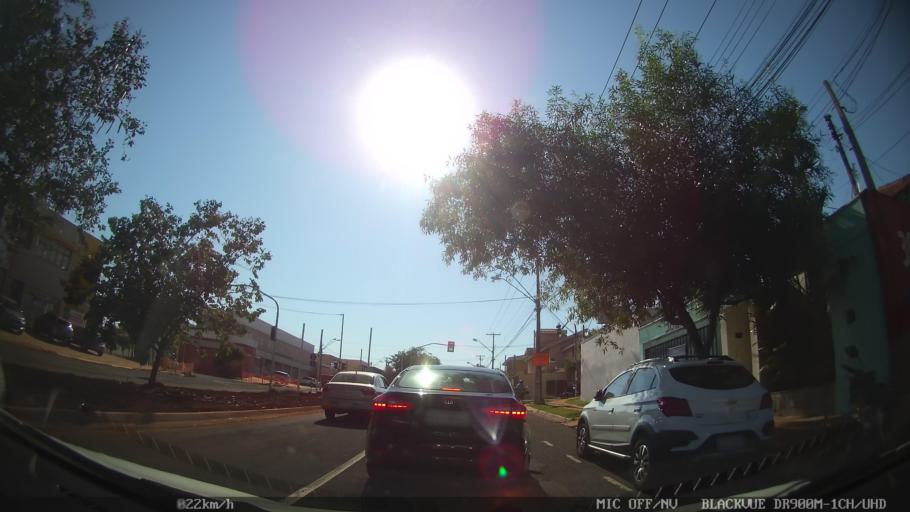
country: BR
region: Sao Paulo
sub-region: Ribeirao Preto
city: Ribeirao Preto
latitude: -21.2011
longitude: -47.8178
